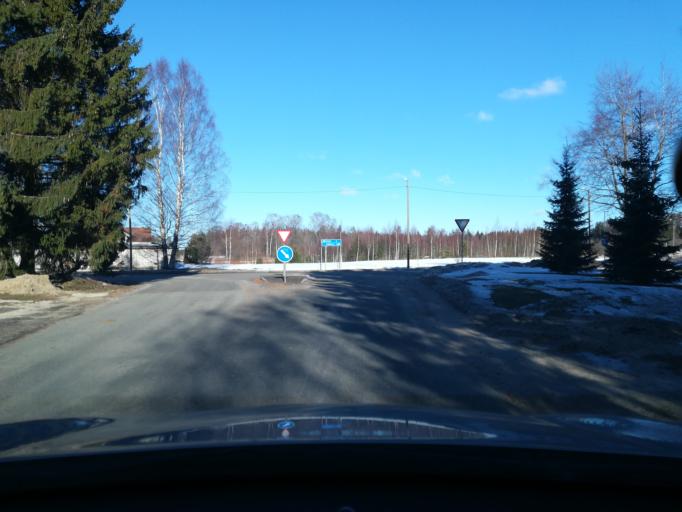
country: EE
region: Raplamaa
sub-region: Kohila vald
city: Kohila
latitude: 59.2289
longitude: 24.7136
